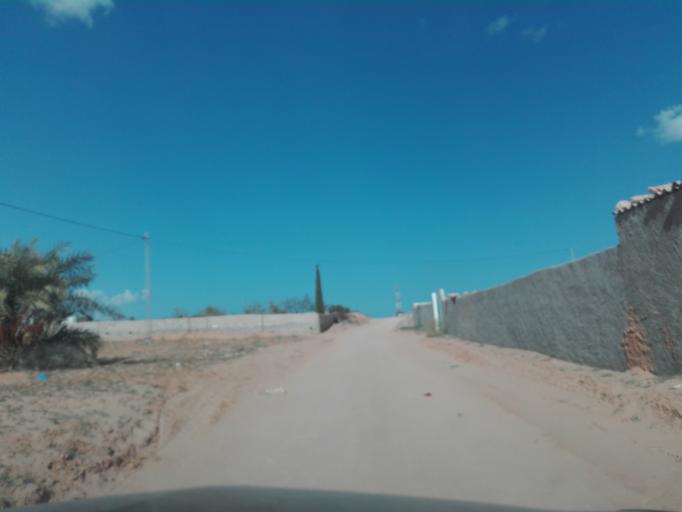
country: TN
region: Madanin
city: Bin Qirdan
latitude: 33.1634
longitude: 11.1957
